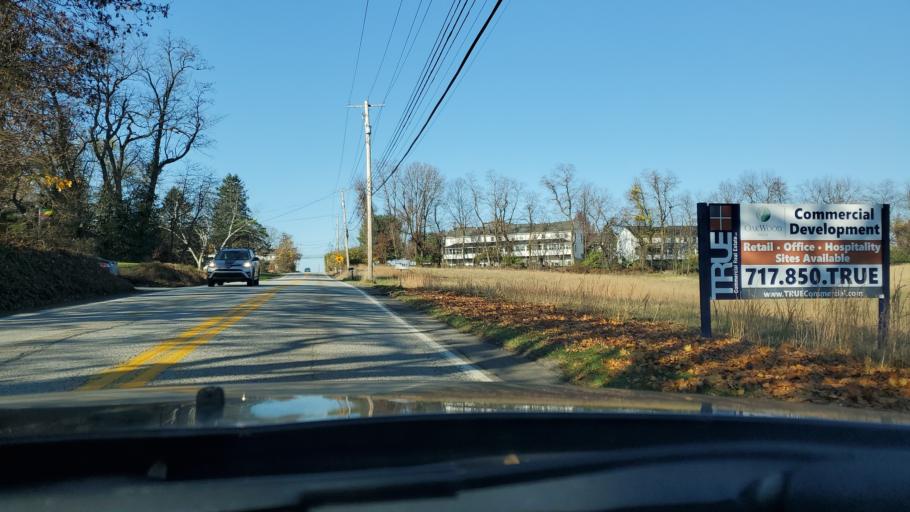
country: US
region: Pennsylvania
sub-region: Cumberland County
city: Mechanicsburg
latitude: 40.1630
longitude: -76.9943
